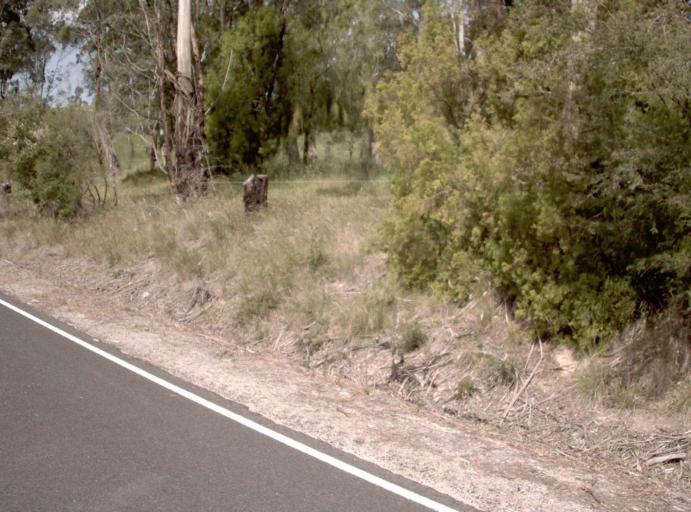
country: AU
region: New South Wales
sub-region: Bega Valley
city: Eden
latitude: -37.4801
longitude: 149.6328
